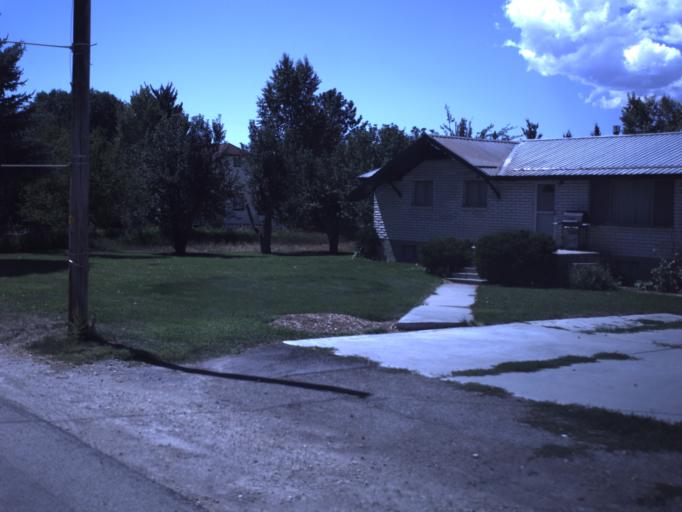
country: US
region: Utah
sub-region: Summit County
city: Oakley
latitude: 40.7145
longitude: -111.3003
